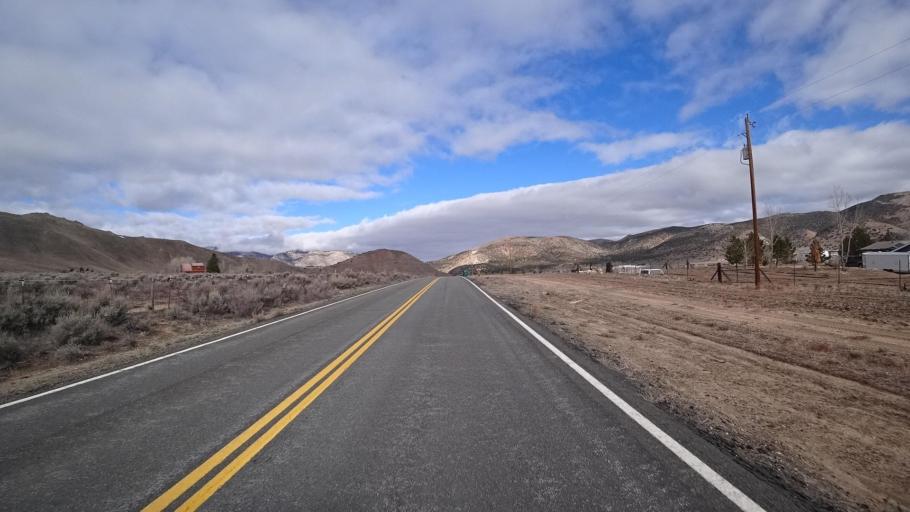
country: US
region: Nevada
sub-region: Washoe County
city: Cold Springs
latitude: 39.8877
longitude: -119.9731
